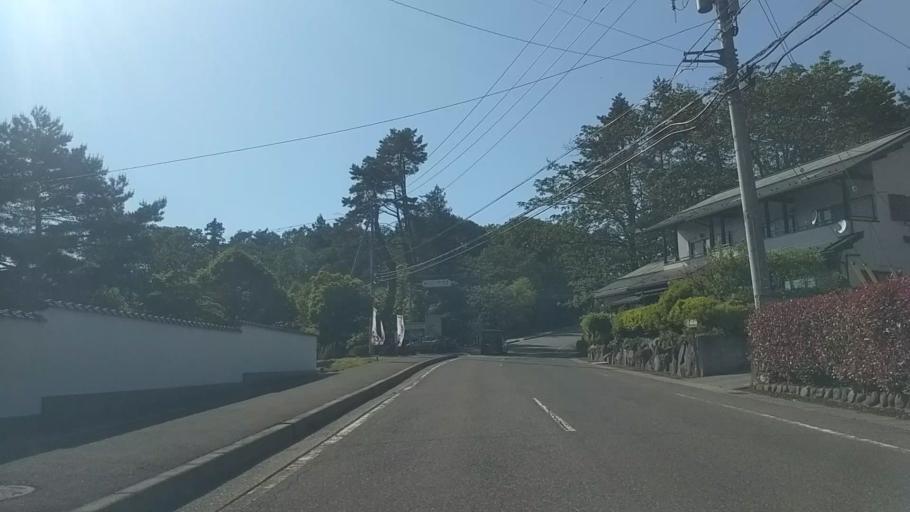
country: JP
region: Yamanashi
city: Nirasaki
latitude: 35.8764
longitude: 138.3567
